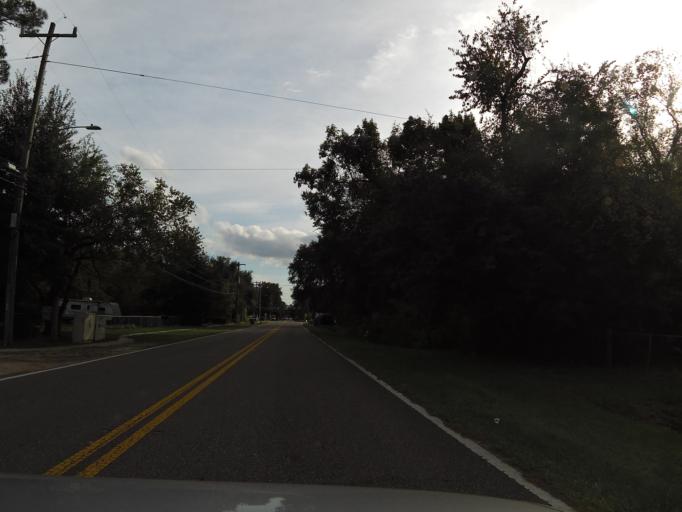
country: US
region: Florida
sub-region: Duval County
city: Jacksonville
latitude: 30.4406
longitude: -81.6931
